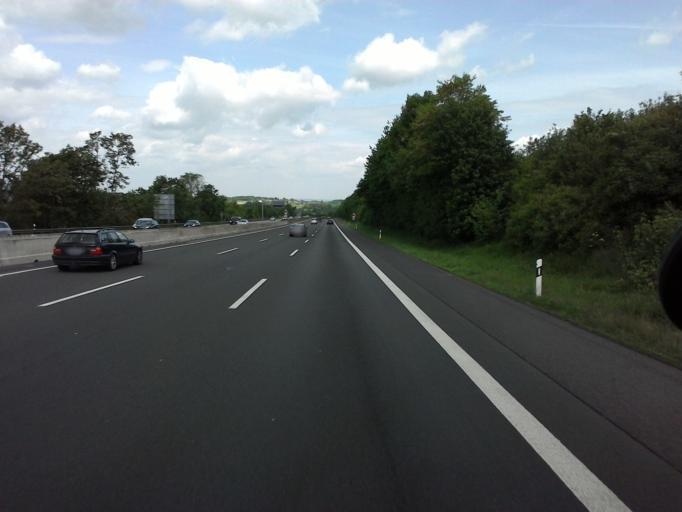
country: DE
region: Rheinland-Pfalz
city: Windhagen
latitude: 50.6565
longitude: 7.3250
